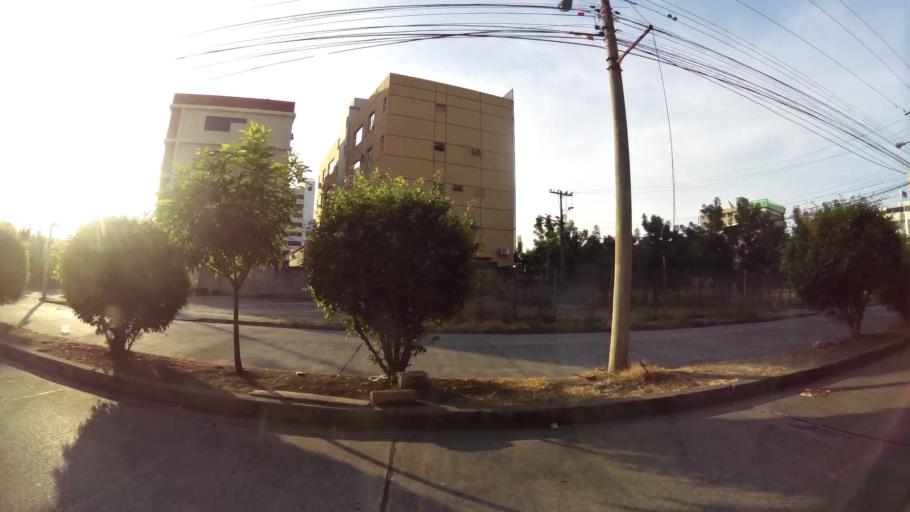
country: EC
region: Guayas
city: Eloy Alfaro
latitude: -2.1592
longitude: -79.8975
